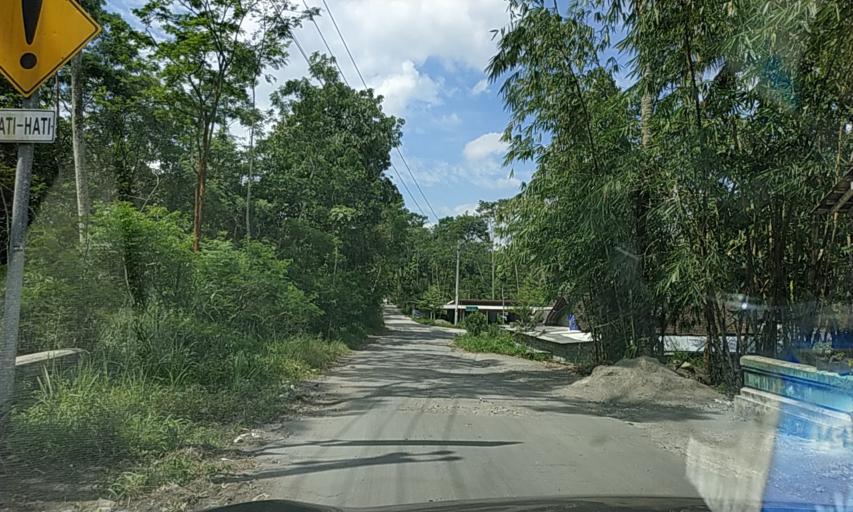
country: ID
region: Central Java
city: Jogonalan
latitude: -7.6284
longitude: 110.4800
